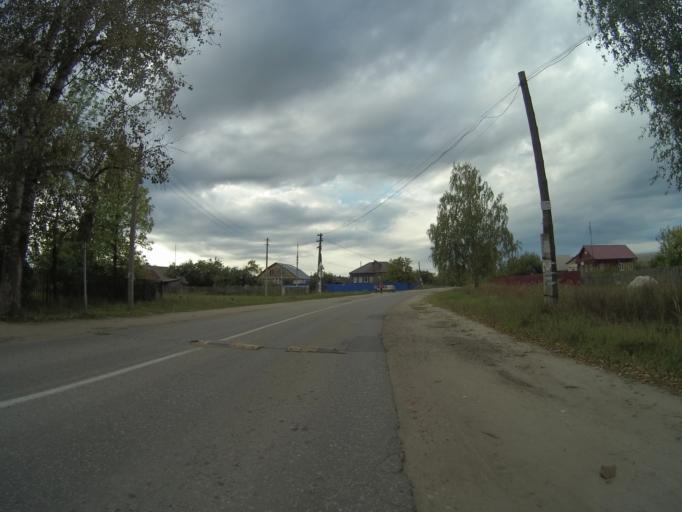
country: RU
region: Vladimir
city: Golovino
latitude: 55.9526
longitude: 40.4330
